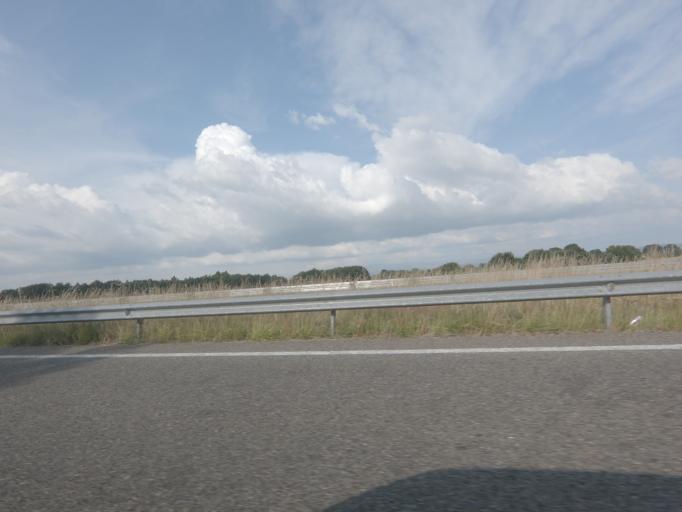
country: ES
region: Galicia
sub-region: Provincia de Ourense
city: Xinzo de Limia
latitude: 42.1326
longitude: -7.7423
